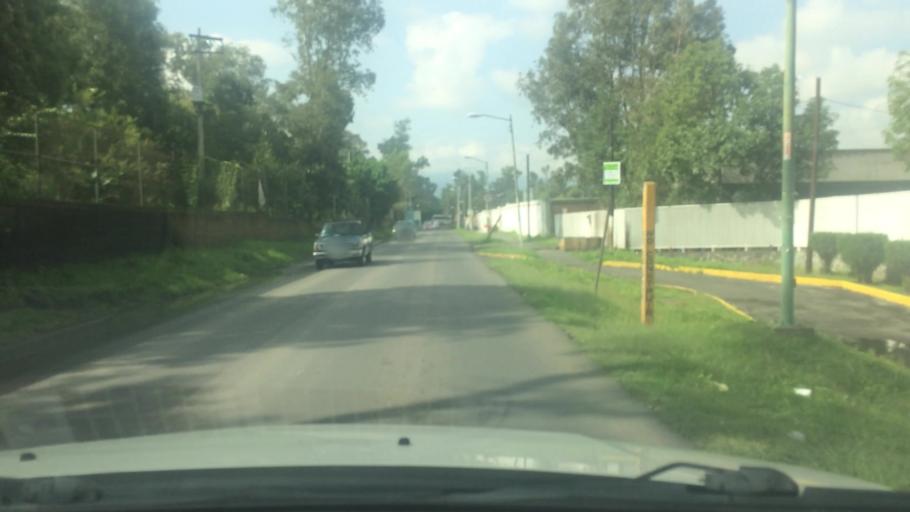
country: MX
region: Mexico City
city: Xochimilco
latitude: 19.3024
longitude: -99.1007
